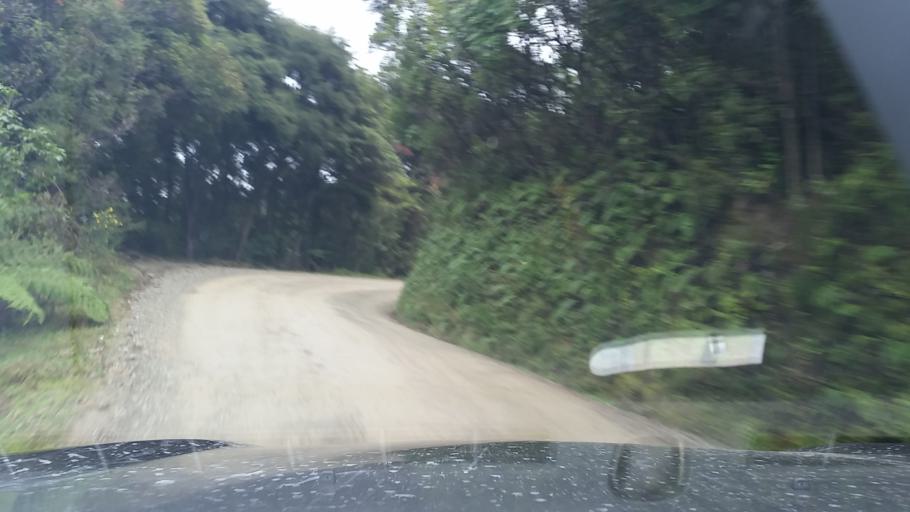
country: NZ
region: Marlborough
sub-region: Marlborough District
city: Picton
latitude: -41.1767
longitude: 174.0790
